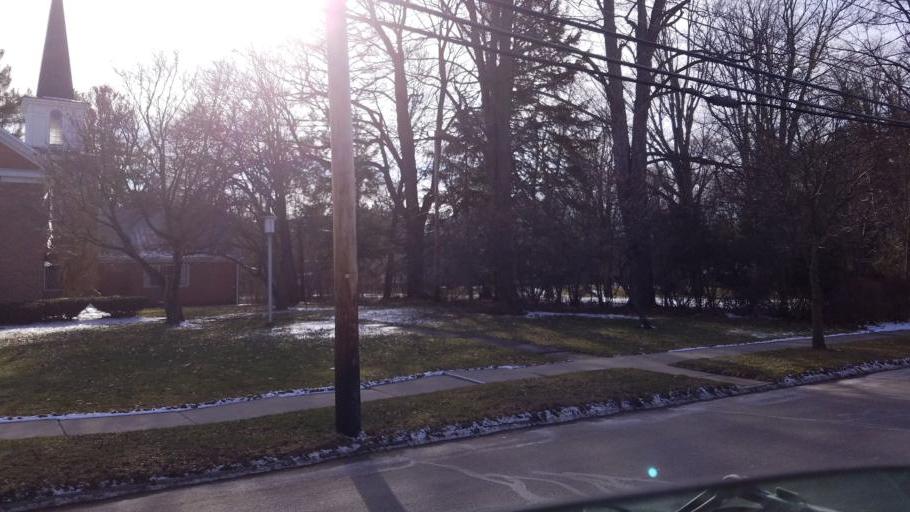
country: US
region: New York
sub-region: Allegany County
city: Wellsville
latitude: 42.1248
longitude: -77.9529
